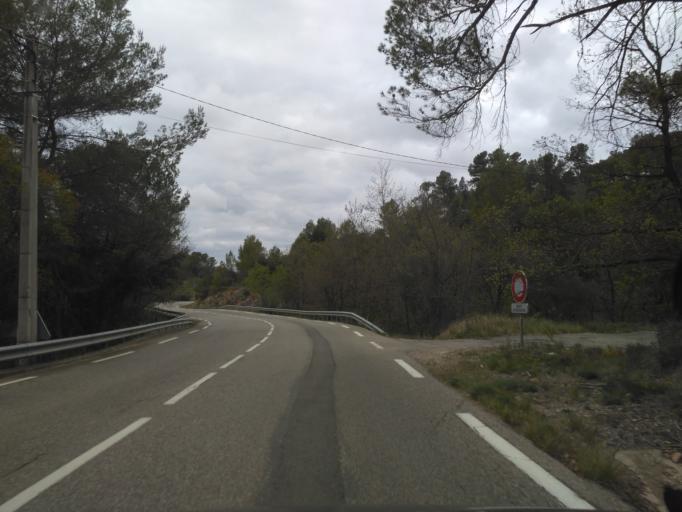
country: FR
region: Provence-Alpes-Cote d'Azur
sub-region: Departement du Var
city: Barjols
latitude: 43.6055
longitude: 5.9546
